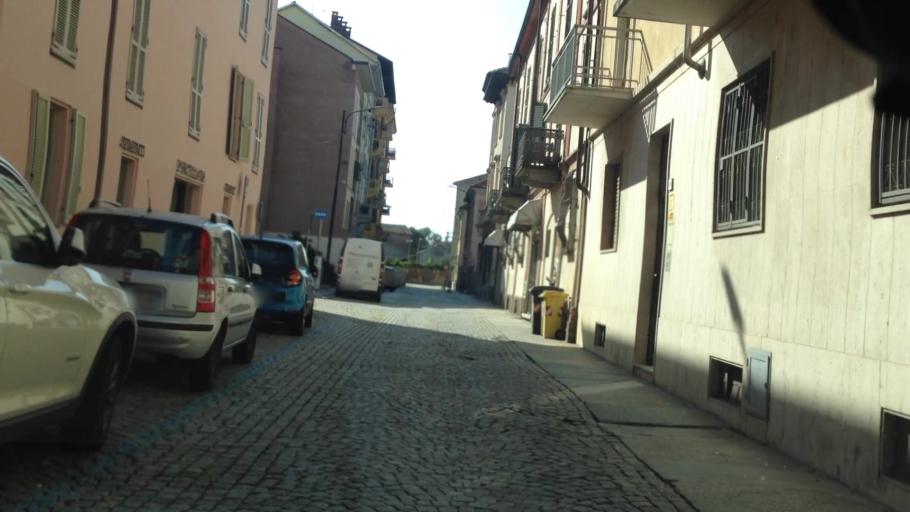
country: IT
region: Piedmont
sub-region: Provincia di Asti
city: Asti
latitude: 44.8954
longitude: 8.2051
